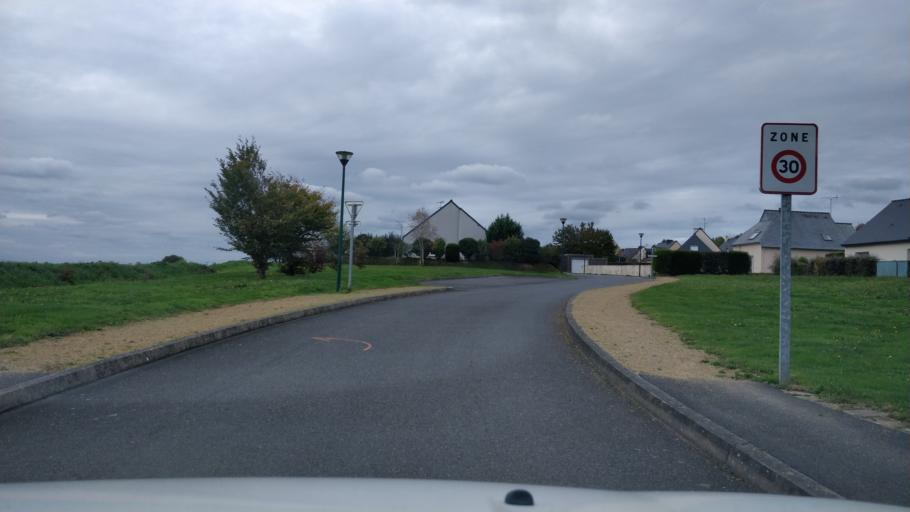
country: FR
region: Brittany
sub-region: Departement des Cotes-d'Armor
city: Minihy-Treguier
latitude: 48.7762
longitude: -3.2311
